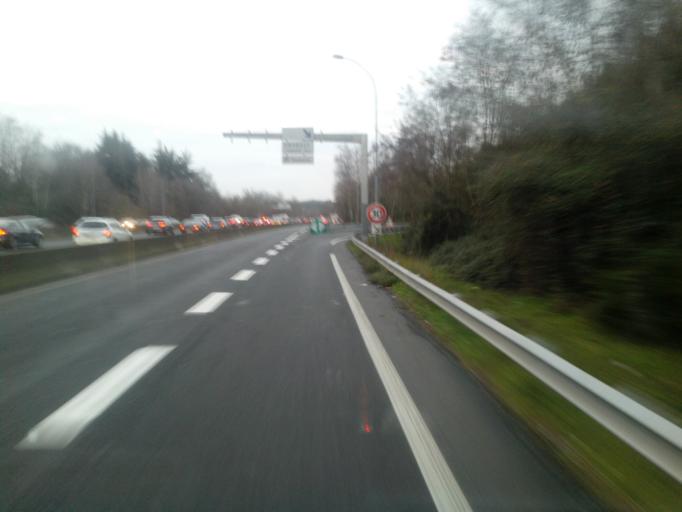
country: FR
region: Pays de la Loire
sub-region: Departement de la Loire-Atlantique
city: Orvault
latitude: 47.2657
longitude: -1.5882
